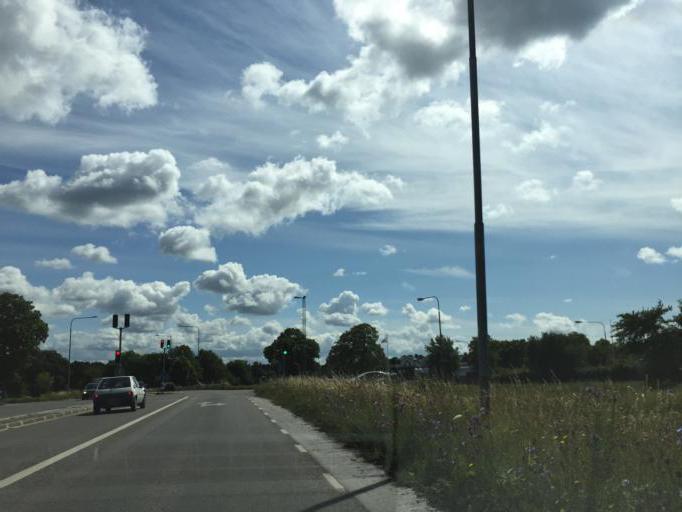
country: SE
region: Gotland
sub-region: Gotland
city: Visby
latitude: 57.6172
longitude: 18.2836
